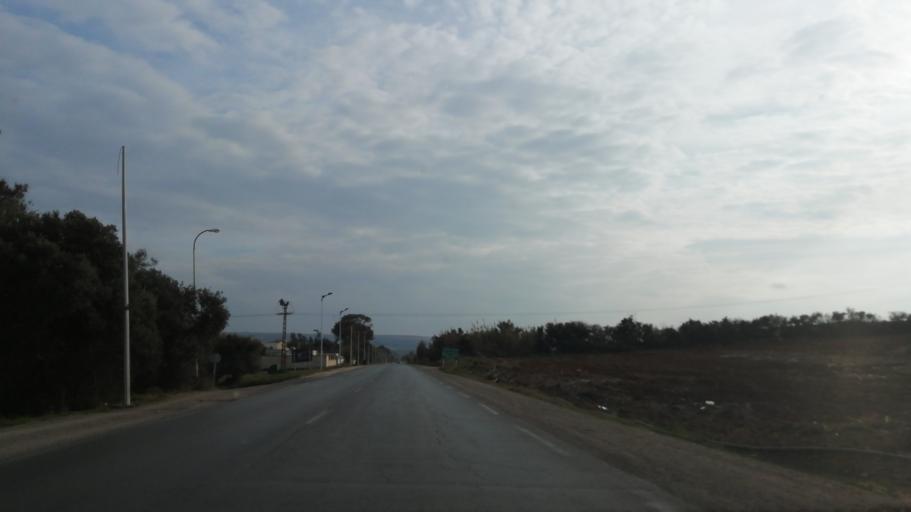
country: DZ
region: Mostaganem
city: Mostaganem
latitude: 35.8855
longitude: 0.0772
